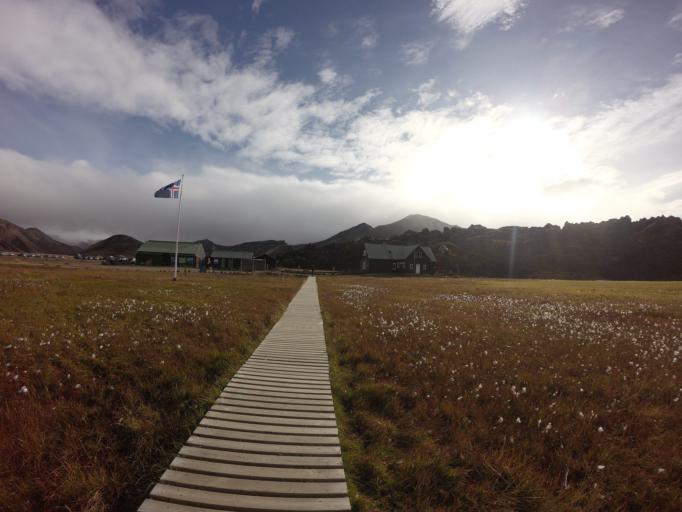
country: IS
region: South
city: Vestmannaeyjar
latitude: 63.9911
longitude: -19.0610
